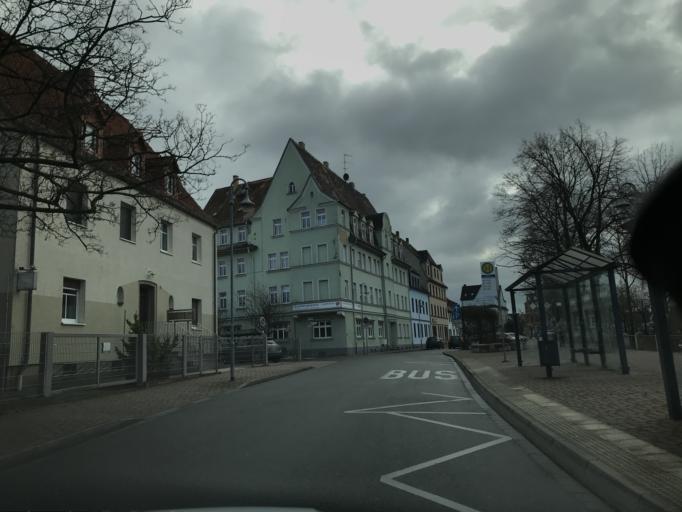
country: DE
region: Saxony
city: Delitzsch
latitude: 51.5250
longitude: 12.3351
